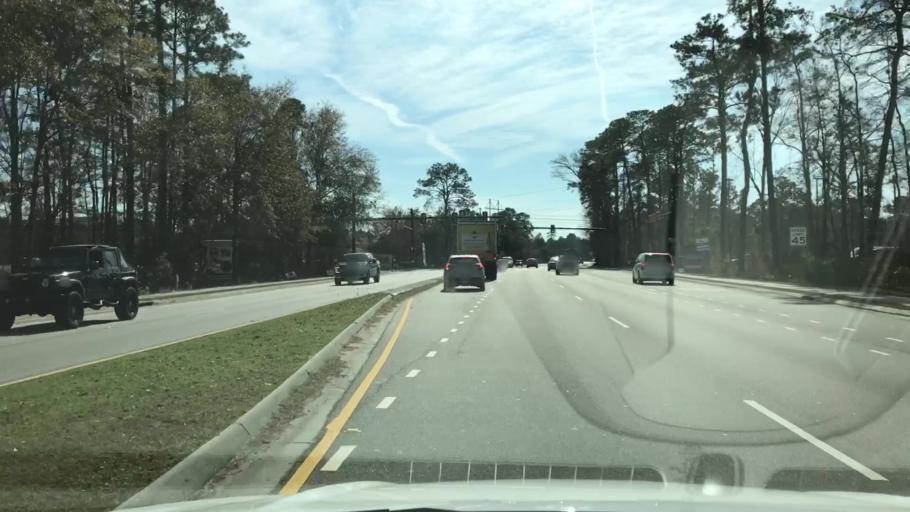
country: US
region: South Carolina
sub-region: Beaufort County
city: Bluffton
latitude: 32.2579
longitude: -80.8535
